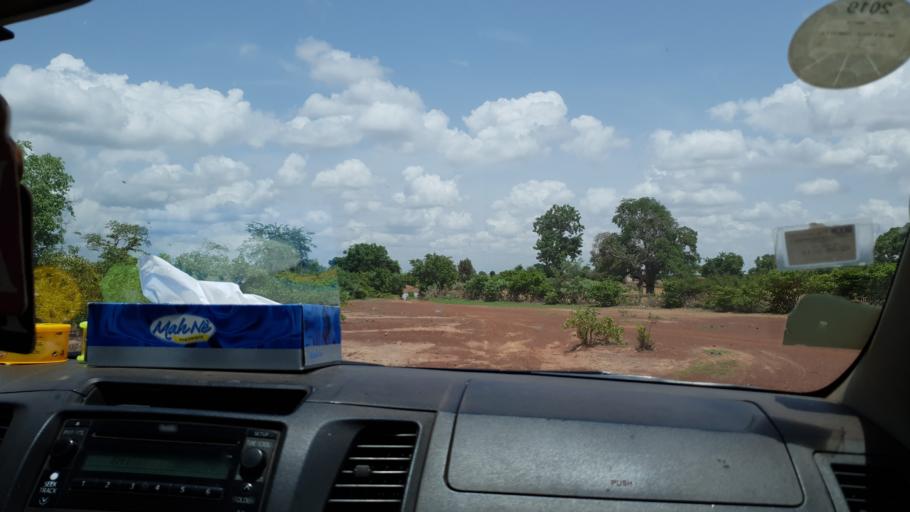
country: ML
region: Koulikoro
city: Banamba
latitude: 13.3778
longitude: -7.2159
